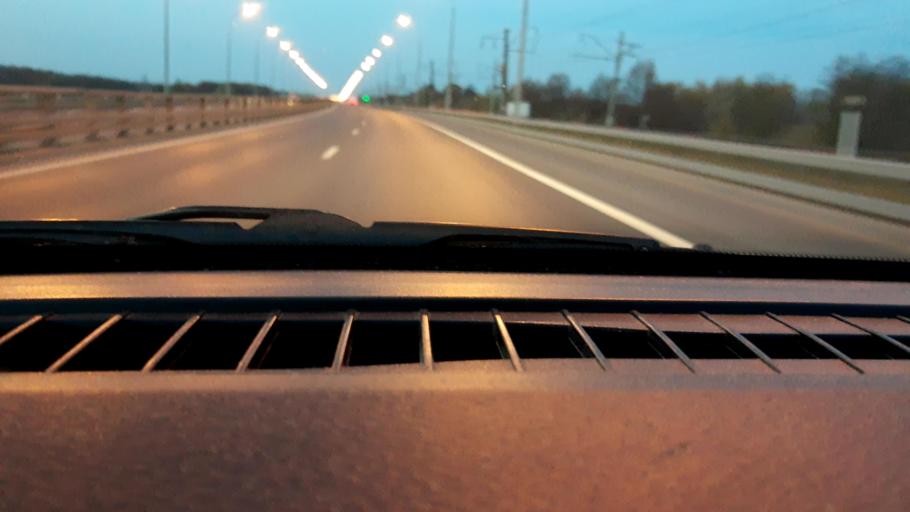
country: RU
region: Nizjnij Novgorod
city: Neklyudovo
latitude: 56.3906
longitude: 43.9744
